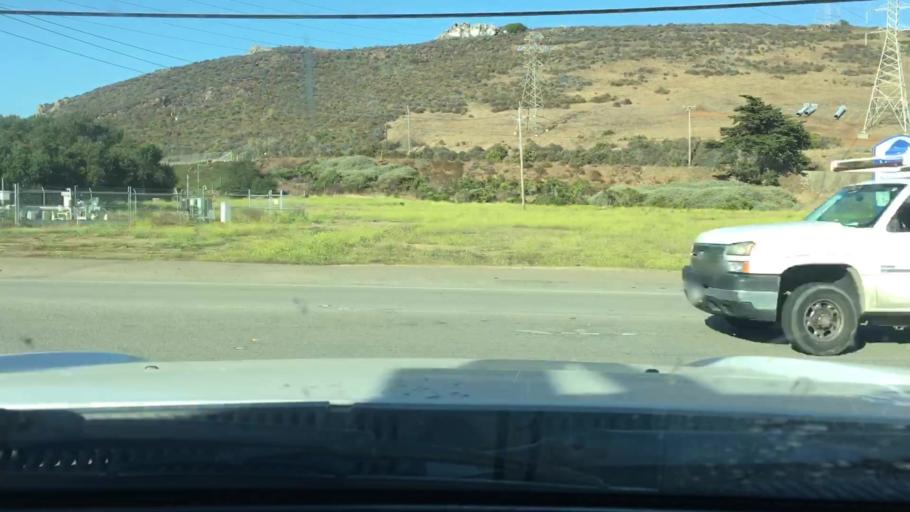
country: US
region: California
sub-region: San Luis Obispo County
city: Morro Bay
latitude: 35.3733
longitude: -120.8483
